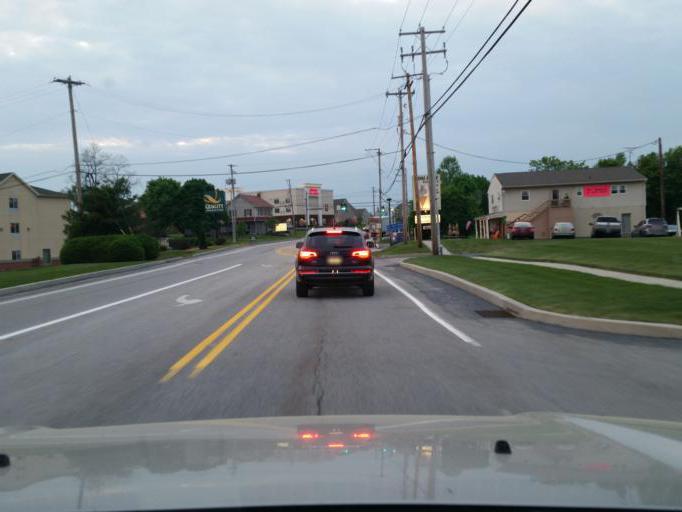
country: US
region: Pennsylvania
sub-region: Dauphin County
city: Hummelstown
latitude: 40.3000
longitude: -76.6898
